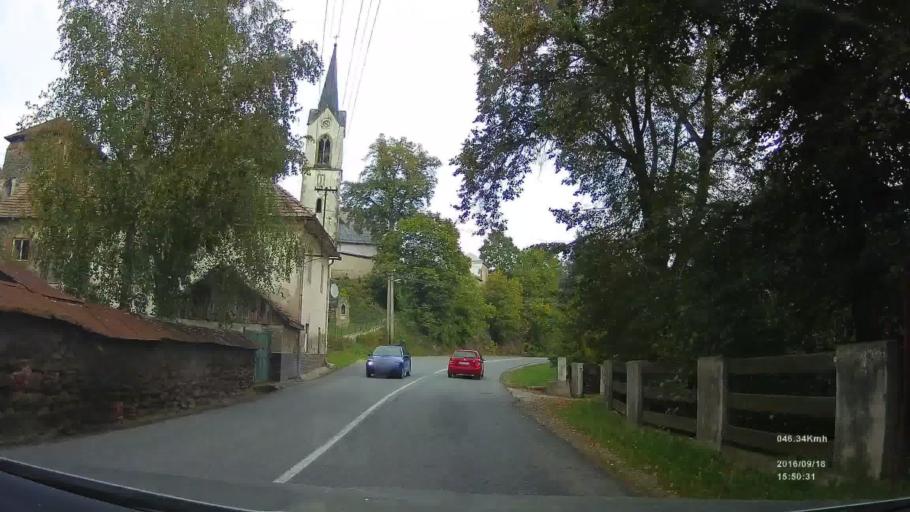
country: SK
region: Kosicky
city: Spisska Nova Ves
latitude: 48.9153
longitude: 20.6196
